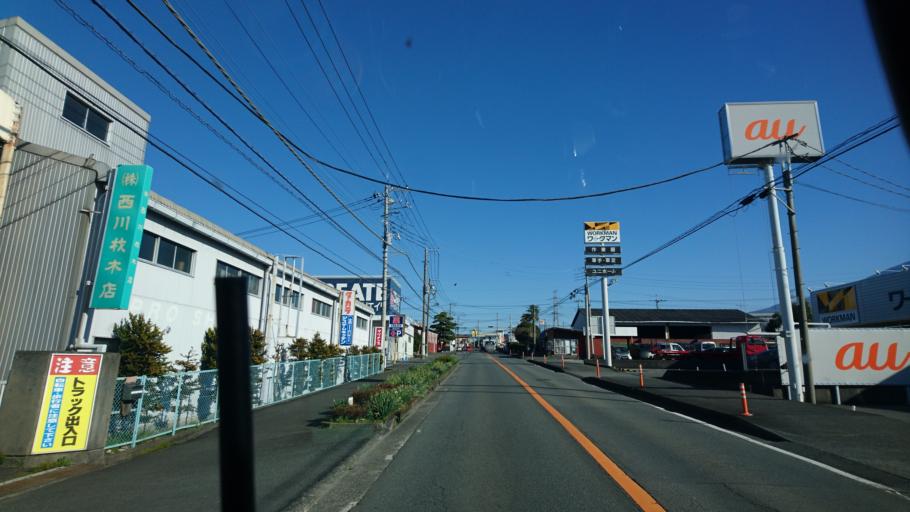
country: JP
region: Shizuoka
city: Fujinomiya
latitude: 35.2489
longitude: 138.6105
